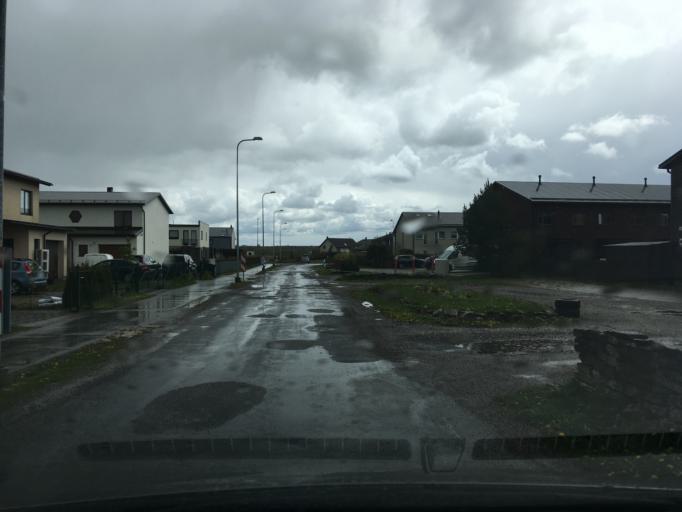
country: EE
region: Harju
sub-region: Joelaehtme vald
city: Loo
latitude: 59.4431
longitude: 24.9622
